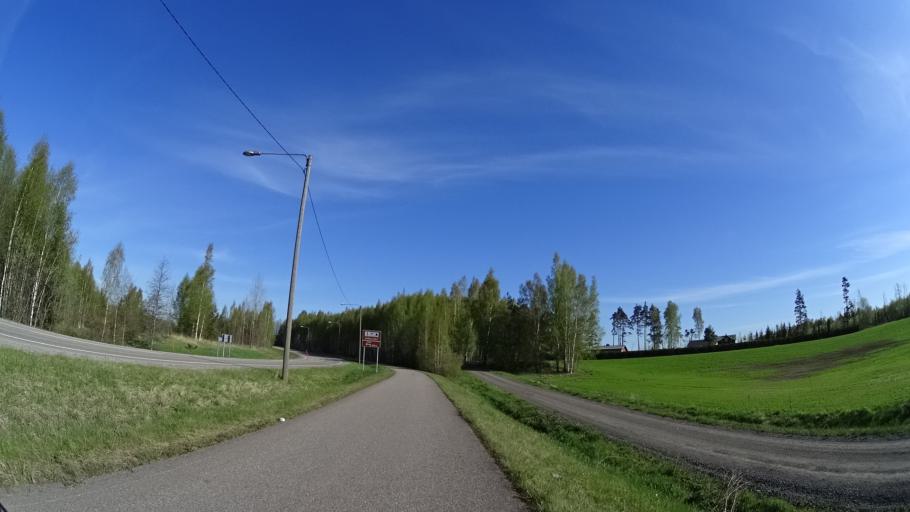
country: FI
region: Uusimaa
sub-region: Helsinki
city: Kilo
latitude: 60.3290
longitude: 24.8253
